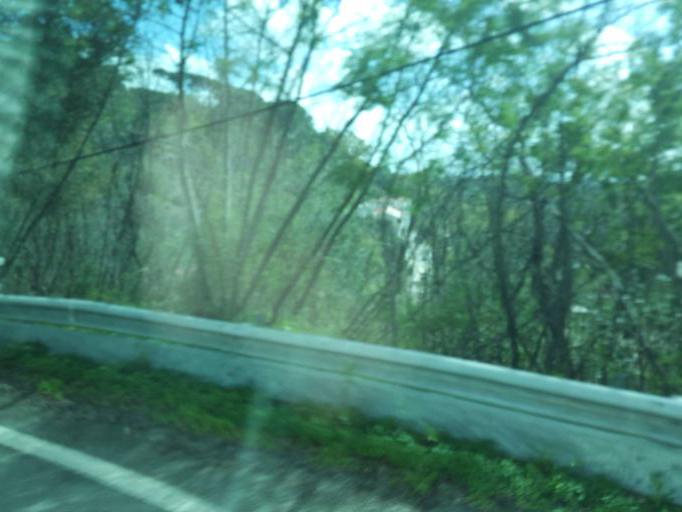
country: PT
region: Faro
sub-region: Monchique
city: Monchique
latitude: 37.2867
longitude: -8.5537
